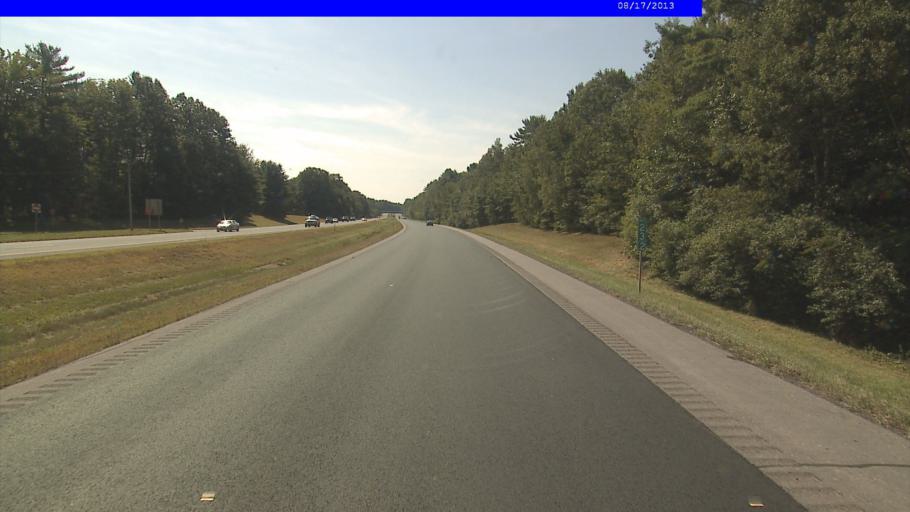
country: US
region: New Hampshire
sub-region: Cheshire County
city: Westmoreland
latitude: 43.0155
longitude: -72.4729
